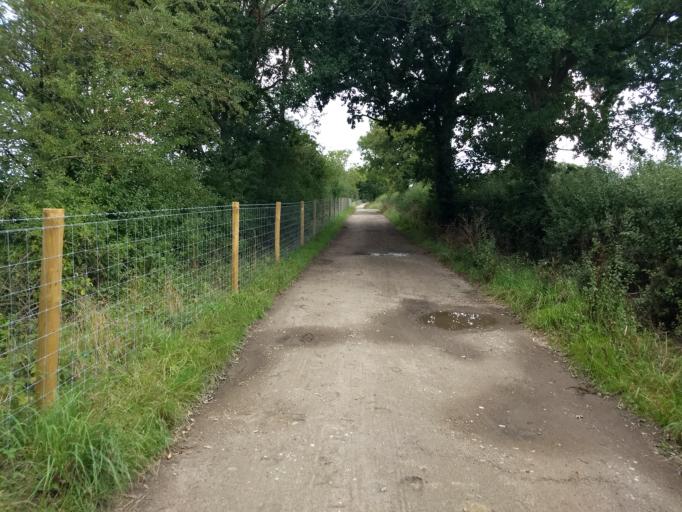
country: GB
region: England
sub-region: Buckinghamshire
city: Winslow
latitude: 51.9605
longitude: -0.8296
